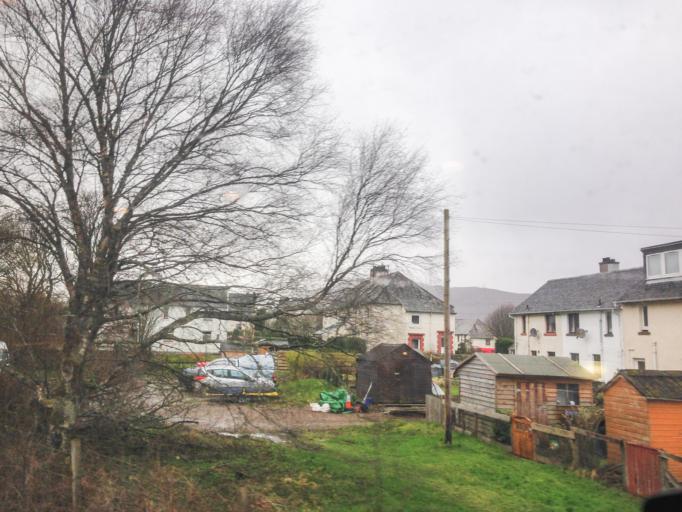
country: GB
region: Scotland
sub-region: Highland
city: Fort William
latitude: 56.8275
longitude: -5.0884
